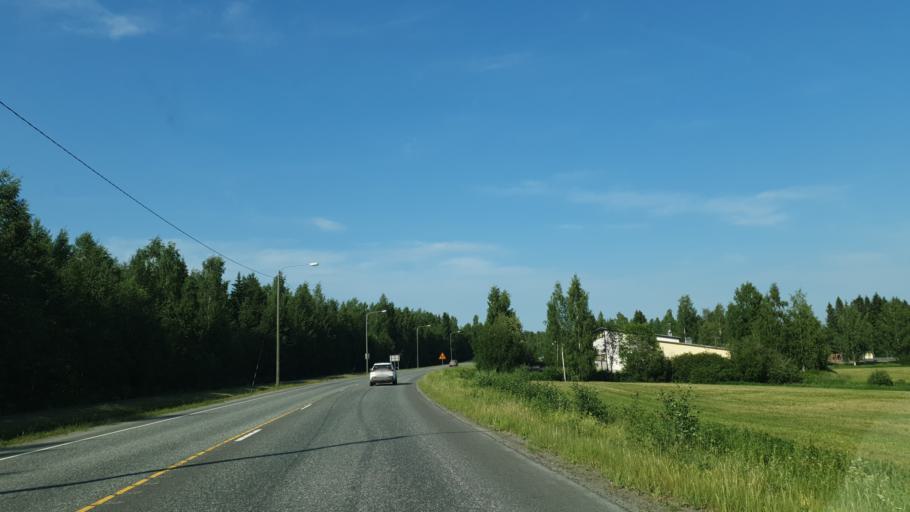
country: FI
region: Northern Savo
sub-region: Kuopio
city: Siilinjaervi
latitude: 63.1292
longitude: 27.7745
